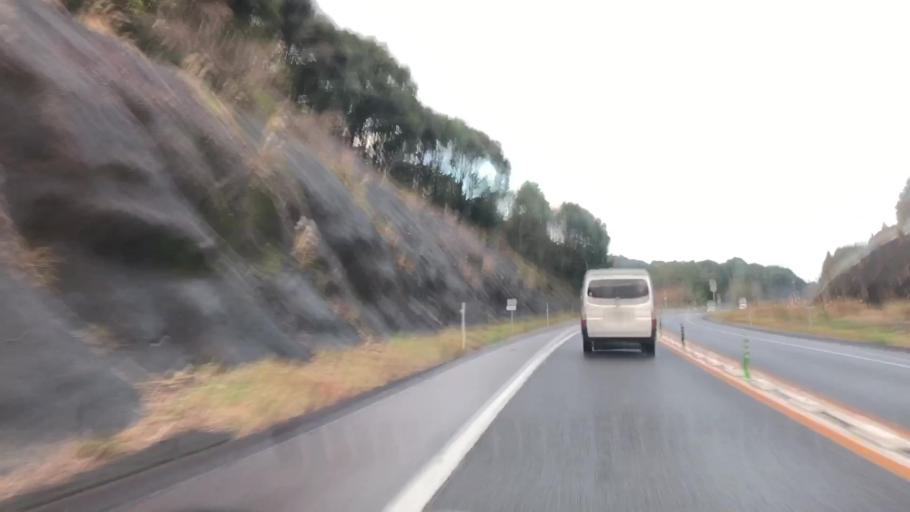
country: JP
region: Saga Prefecture
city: Ureshinomachi-shimojuku
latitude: 33.1433
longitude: 129.9559
